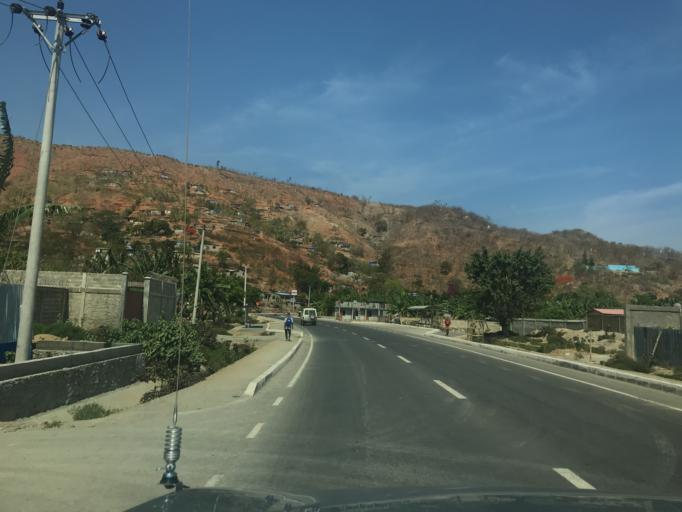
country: TL
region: Dili
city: Dili
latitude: -8.5619
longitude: 125.5255
